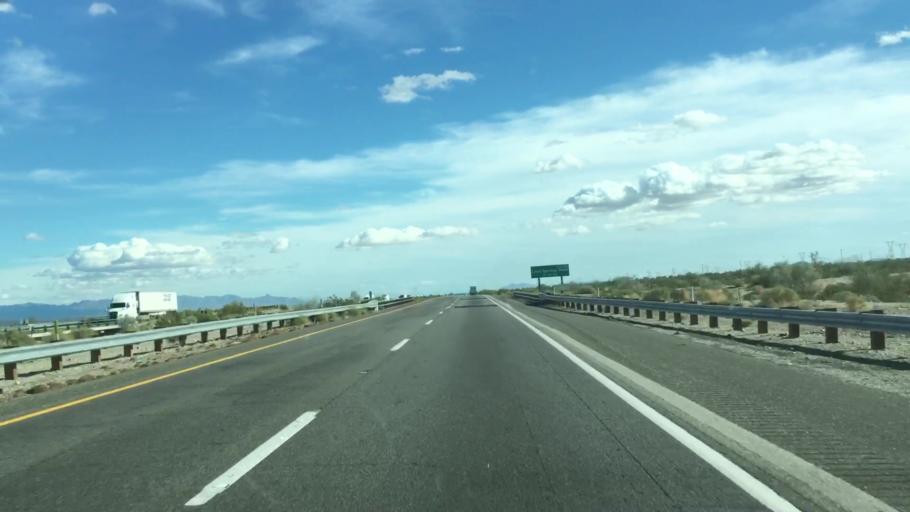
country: US
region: California
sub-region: Imperial County
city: Niland
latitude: 33.6927
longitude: -115.2788
